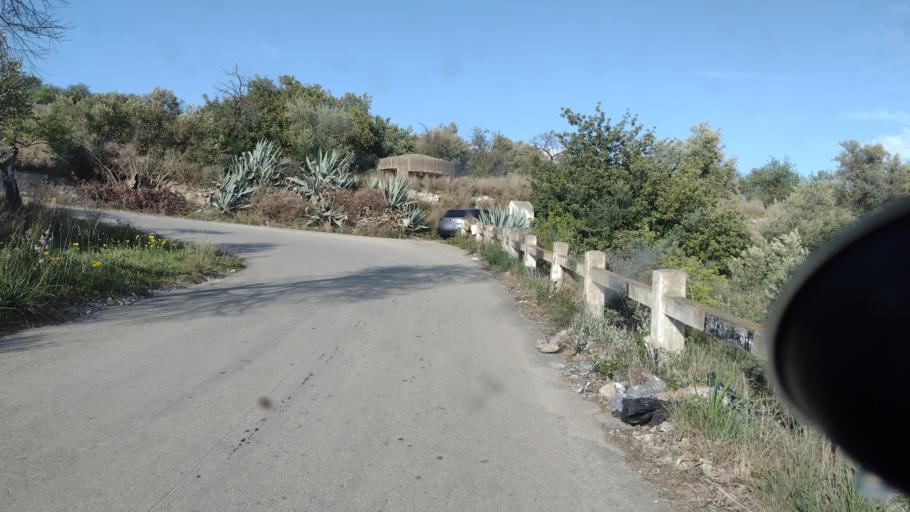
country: IT
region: Sicily
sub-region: Provincia di Siracusa
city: Noto
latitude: 36.8504
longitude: 15.0256
